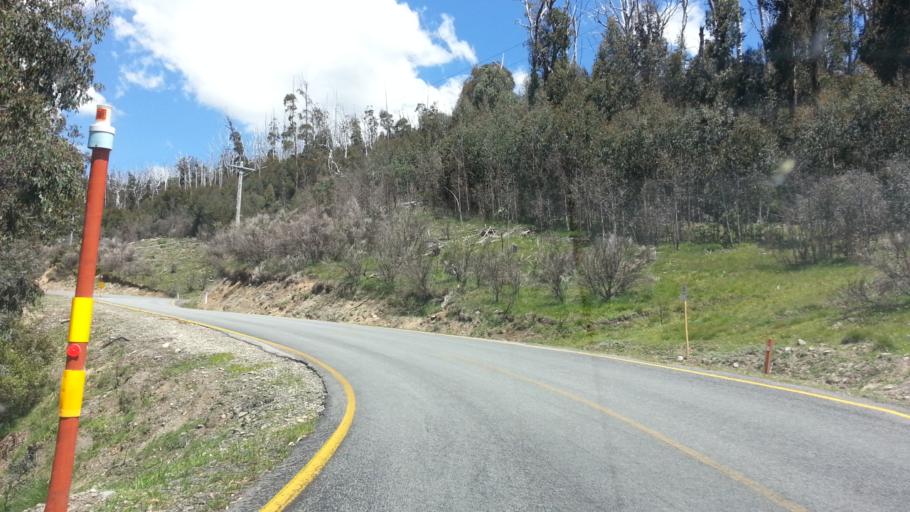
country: AU
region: Victoria
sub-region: Alpine
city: Mount Beauty
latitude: -36.8444
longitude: 147.2650
